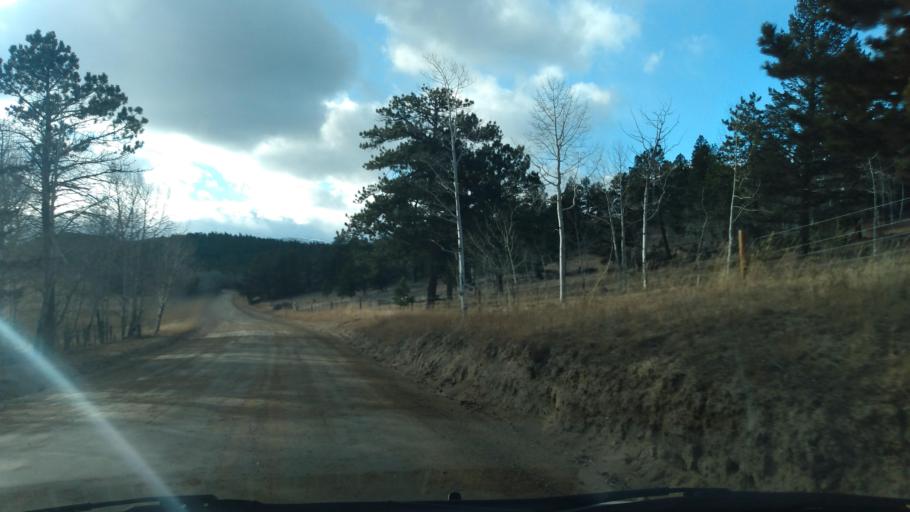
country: US
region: Colorado
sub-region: Boulder County
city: Nederland
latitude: 39.9536
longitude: -105.4618
